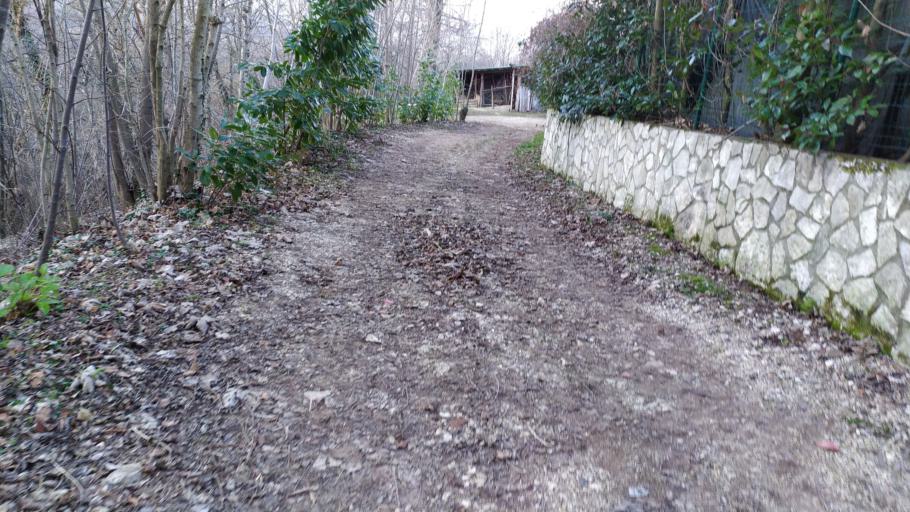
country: IT
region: Veneto
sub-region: Provincia di Vicenza
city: Monte di Malo
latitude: 45.6711
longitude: 11.3489
